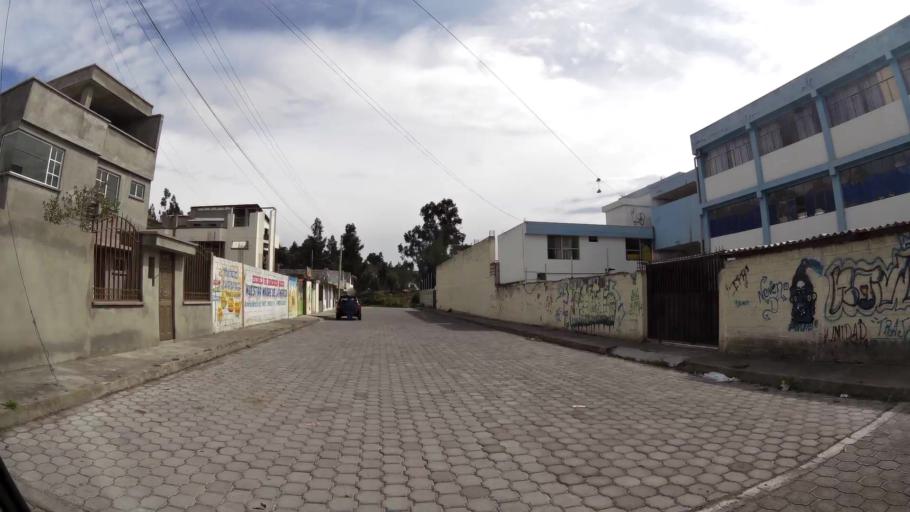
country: EC
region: Cotopaxi
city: Latacunga
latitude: -0.9338
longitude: -78.6020
